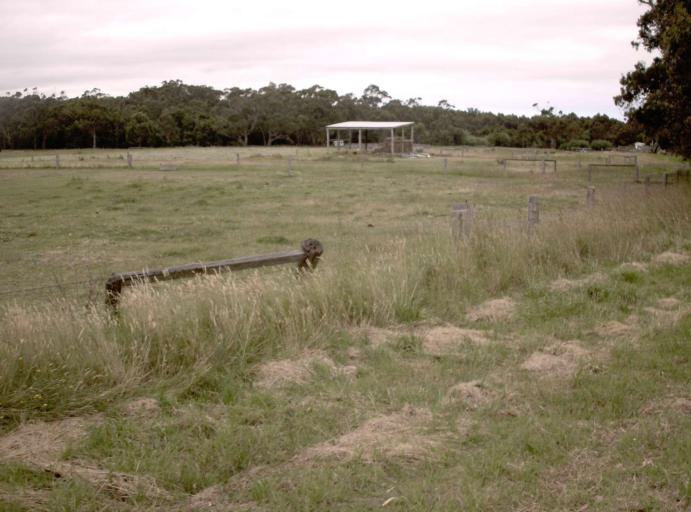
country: AU
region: Victoria
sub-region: Wellington
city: Sale
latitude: -38.5242
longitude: 146.8643
